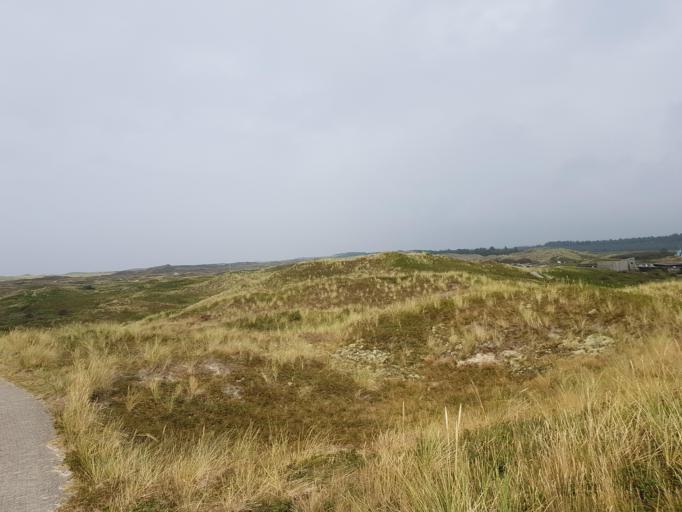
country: NL
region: North Holland
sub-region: Gemeente Texel
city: Den Burg
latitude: 53.0771
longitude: 4.7415
